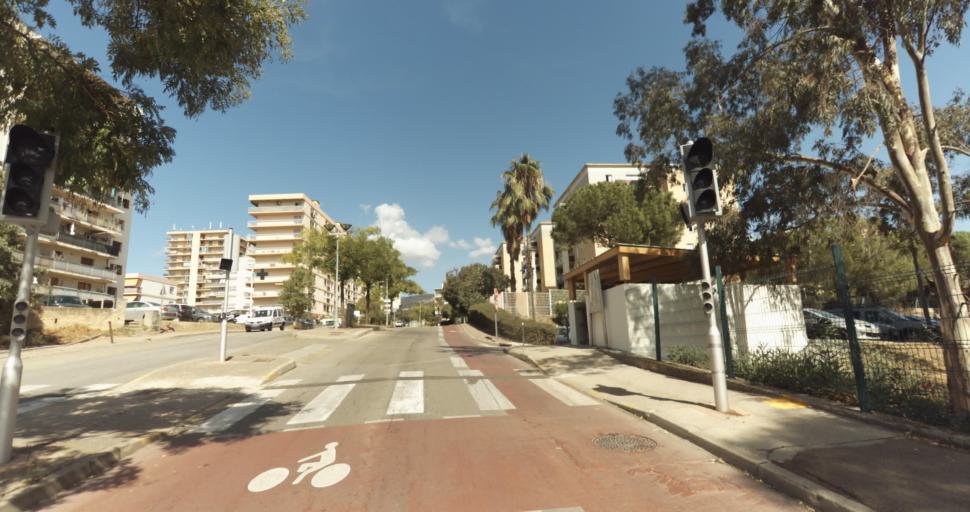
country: FR
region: Corsica
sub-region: Departement de la Corse-du-Sud
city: Ajaccio
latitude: 41.9386
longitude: 8.7510
